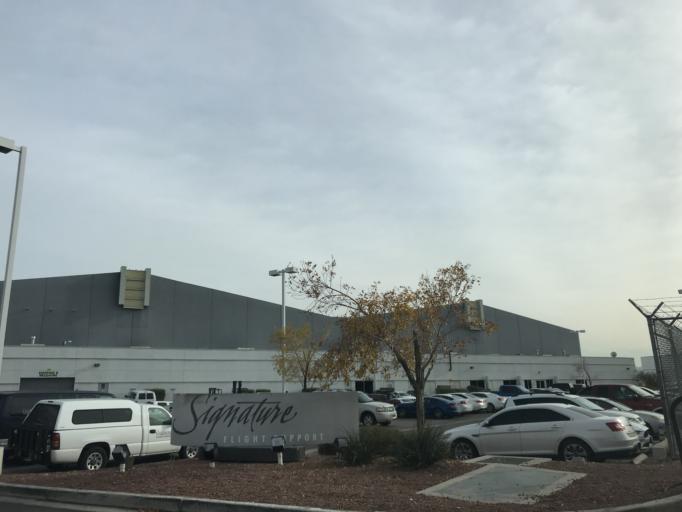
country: US
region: Nevada
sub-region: Clark County
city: Paradise
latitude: 36.0879
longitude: -115.1683
